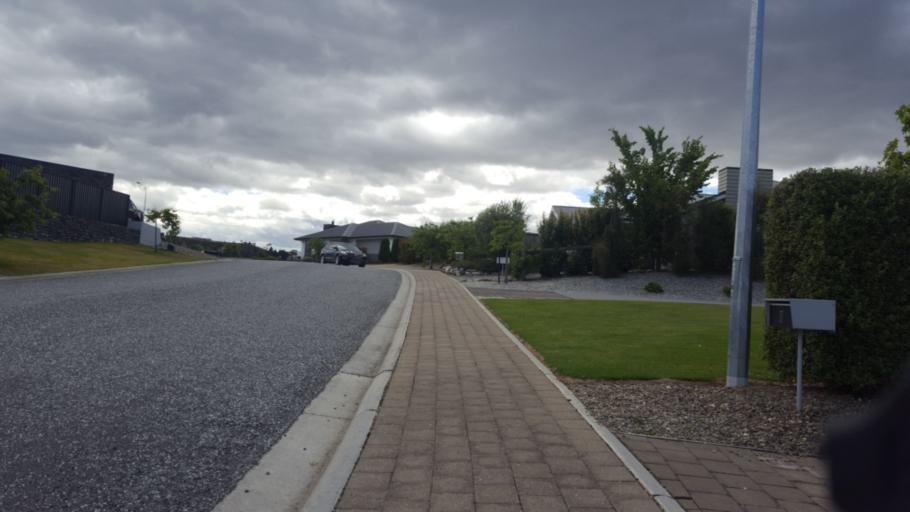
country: NZ
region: Otago
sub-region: Queenstown-Lakes District
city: Wanaka
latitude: -45.1980
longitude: 169.3331
